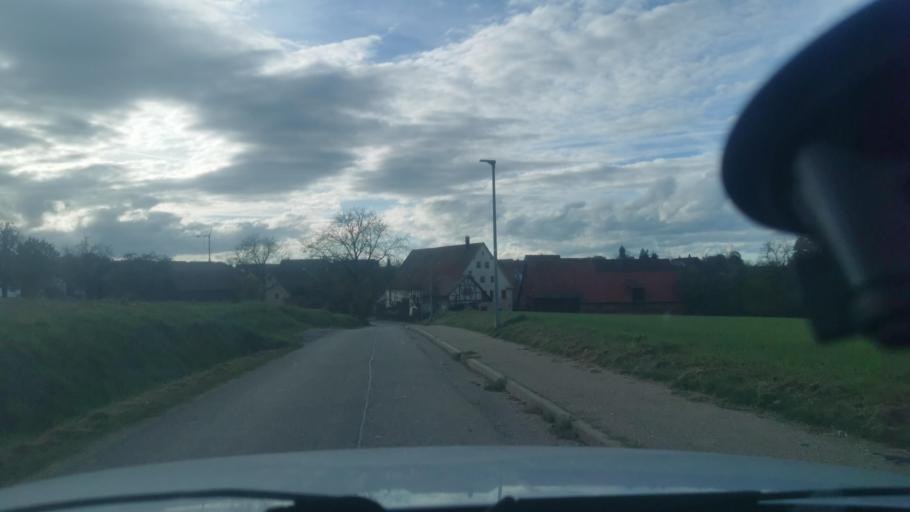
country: DE
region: Baden-Wuerttemberg
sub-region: Regierungsbezirk Stuttgart
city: Eschenbach
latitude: 48.6531
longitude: 9.6751
